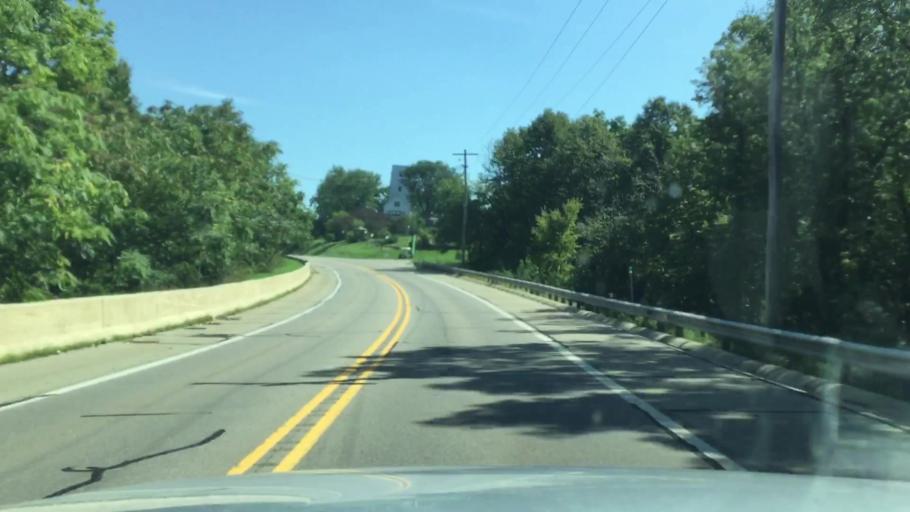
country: US
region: Michigan
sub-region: Jackson County
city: Brooklyn
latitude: 42.0561
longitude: -84.1595
